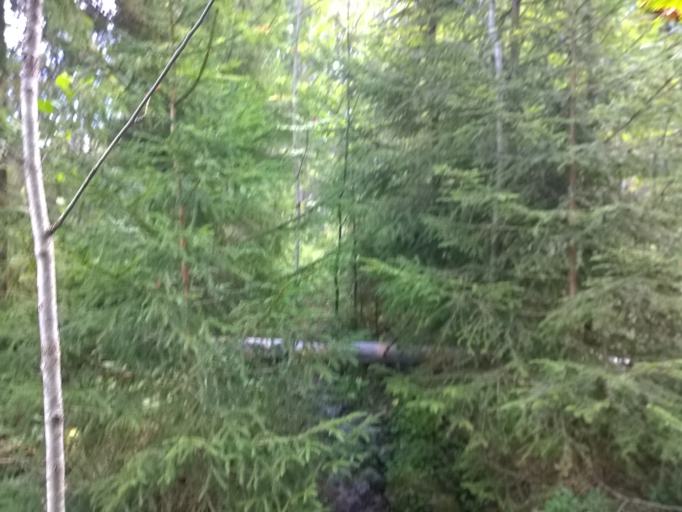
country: FI
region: Pirkanmaa
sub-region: Tampere
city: Tampere
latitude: 61.4475
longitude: 23.8233
